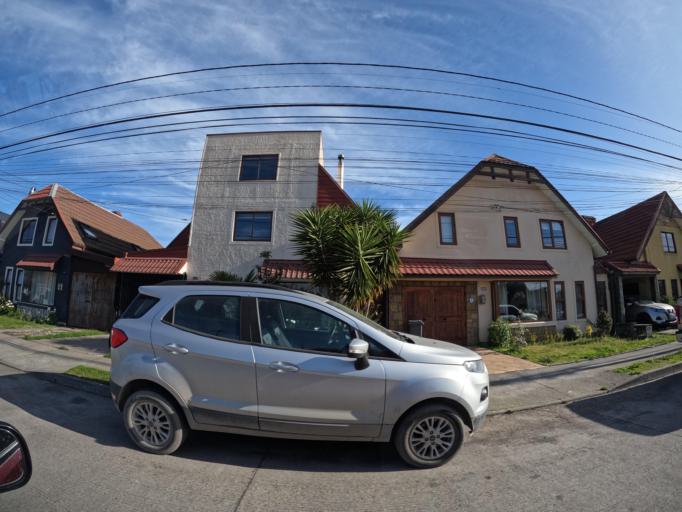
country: CL
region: Biobio
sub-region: Provincia de Concepcion
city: Concepcion
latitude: -36.7729
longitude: -73.0770
